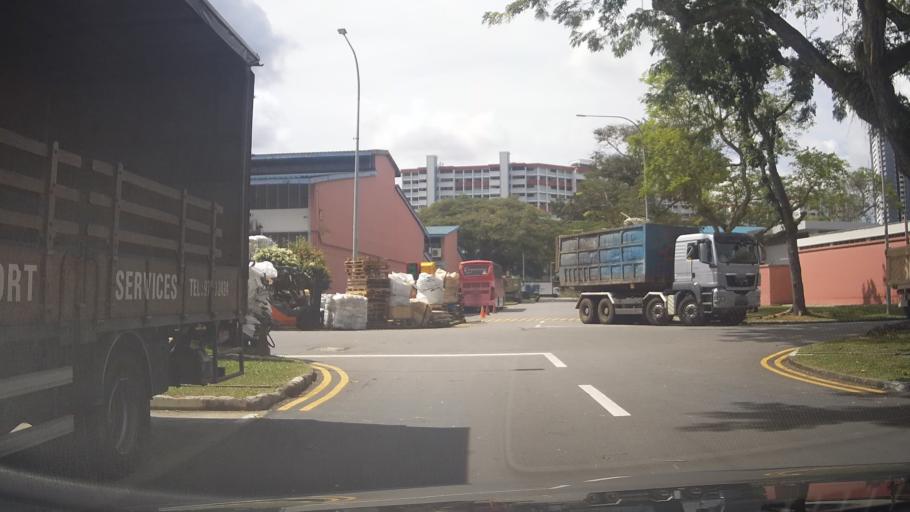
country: MY
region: Johor
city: Johor Bahru
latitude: 1.4411
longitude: 103.7822
